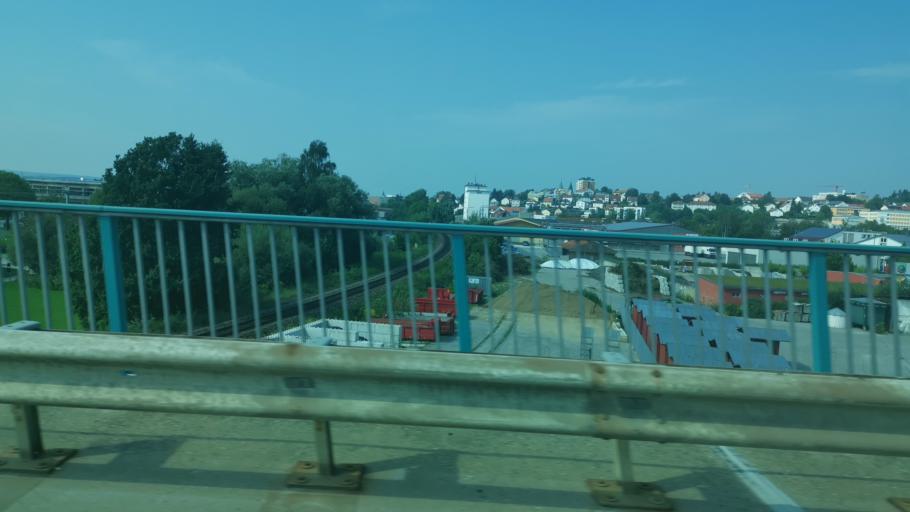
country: DE
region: Bavaria
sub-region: Upper Palatinate
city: Cham
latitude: 49.2233
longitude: 12.6785
